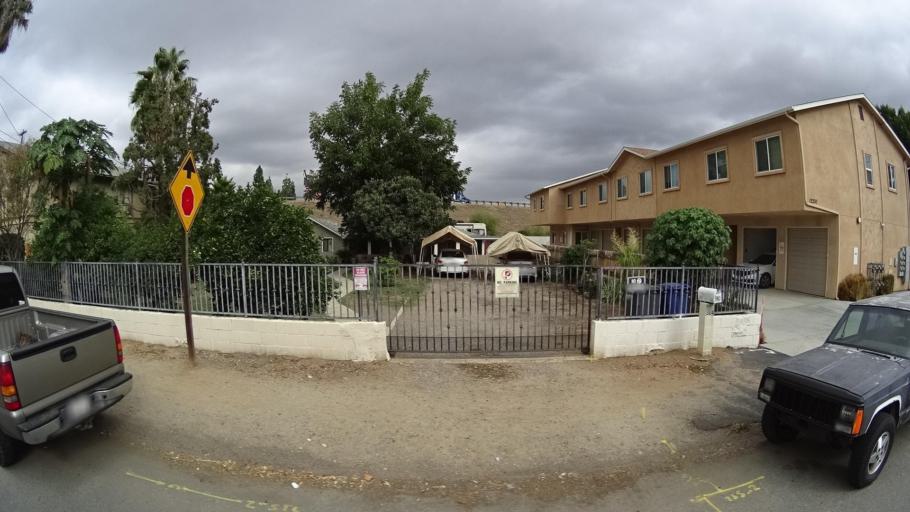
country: US
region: California
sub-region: San Diego County
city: Lakeside
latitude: 32.8595
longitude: -116.9250
